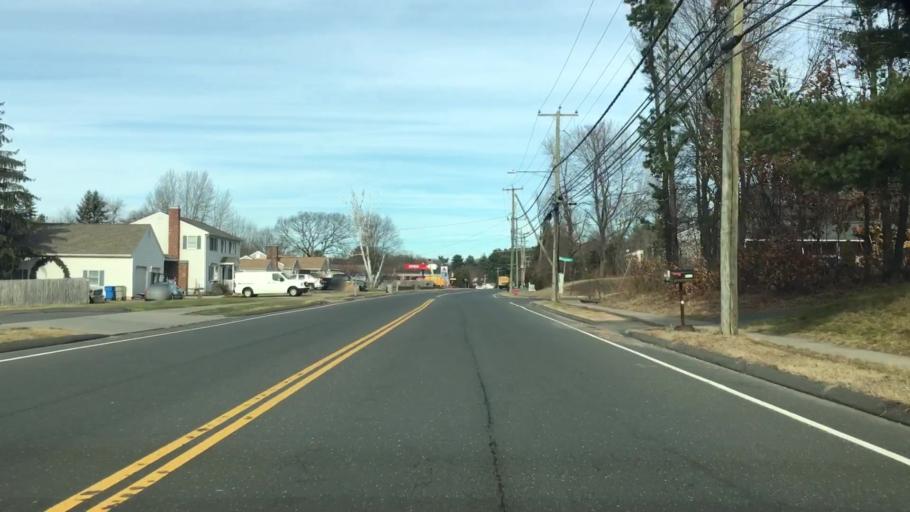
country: US
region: Connecticut
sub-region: Hartford County
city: Plainville
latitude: 41.6555
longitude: -72.9013
